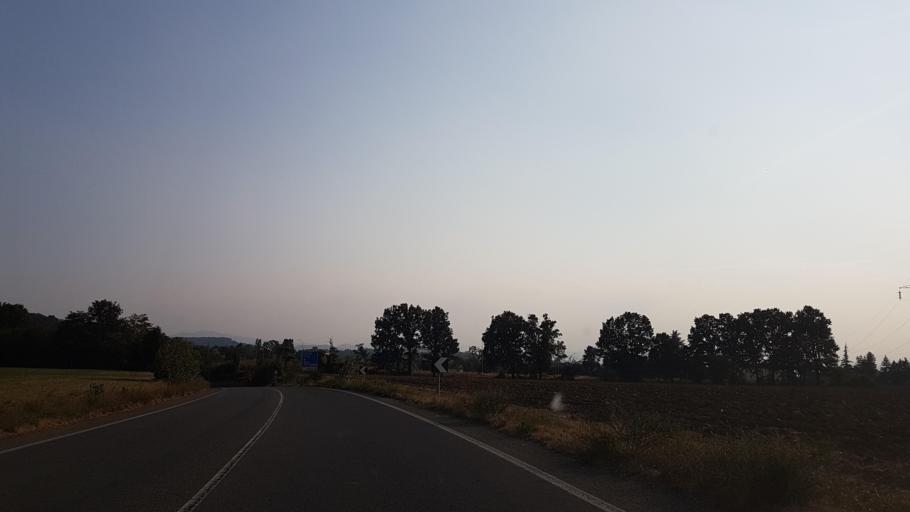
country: IT
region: Emilia-Romagna
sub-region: Provincia di Parma
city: Collecchio
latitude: 44.7482
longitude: 10.1975
